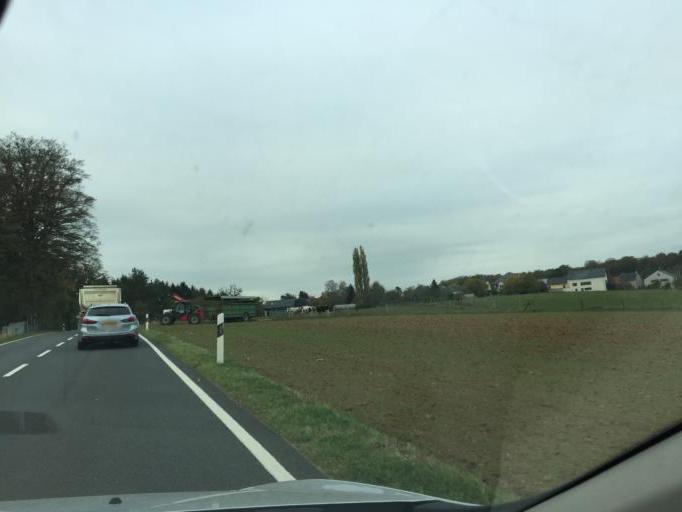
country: LU
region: Luxembourg
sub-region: Canton de Capellen
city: Kopstal
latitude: 49.6991
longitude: 6.0733
